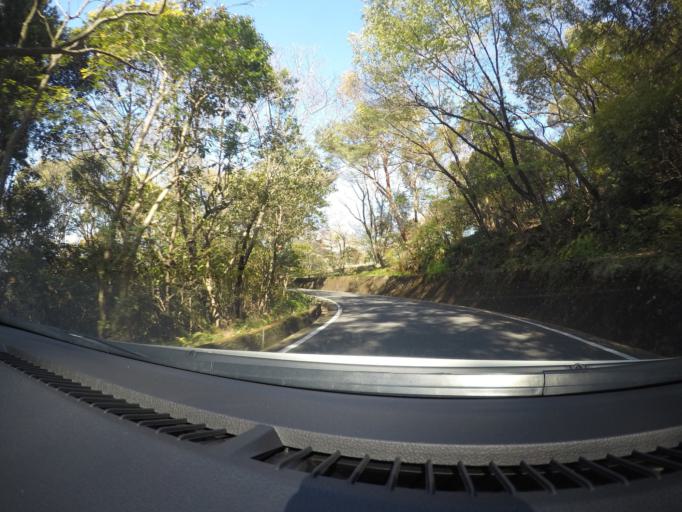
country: JP
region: Kochi
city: Kochi-shi
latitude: 33.5496
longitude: 133.5740
